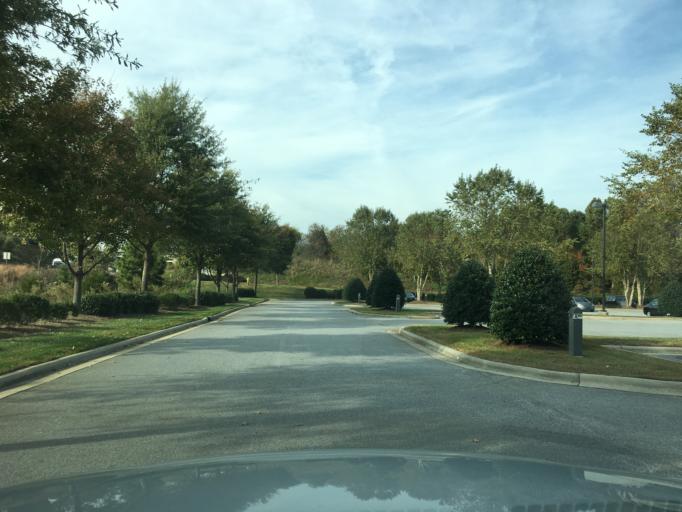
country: US
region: North Carolina
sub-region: Catawba County
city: Saint Stephens
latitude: 35.7301
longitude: -81.2900
